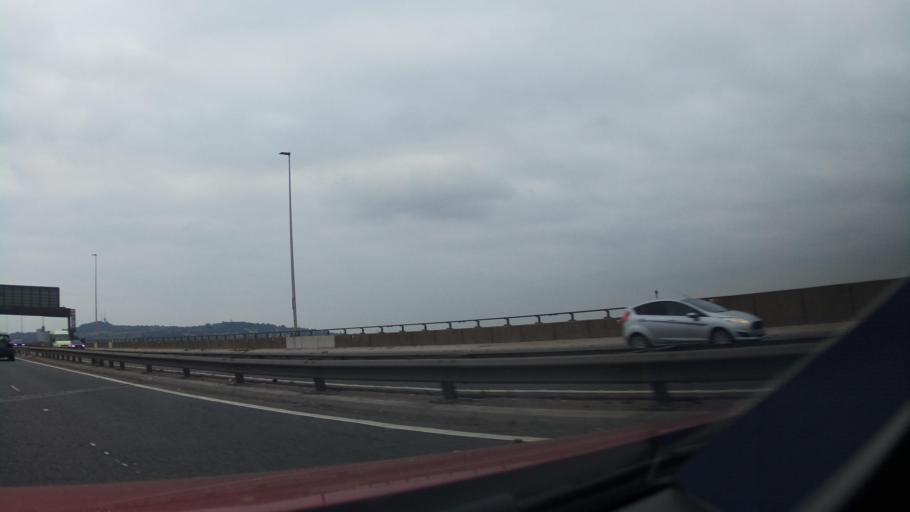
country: GB
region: England
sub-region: Sandwell
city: West Bromwich
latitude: 52.5065
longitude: -1.9988
